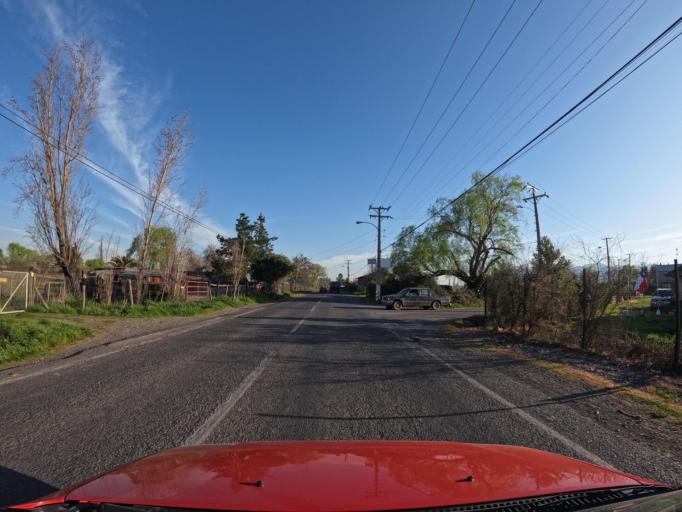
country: CL
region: Maule
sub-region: Provincia de Curico
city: Rauco
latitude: -34.8750
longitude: -71.2674
